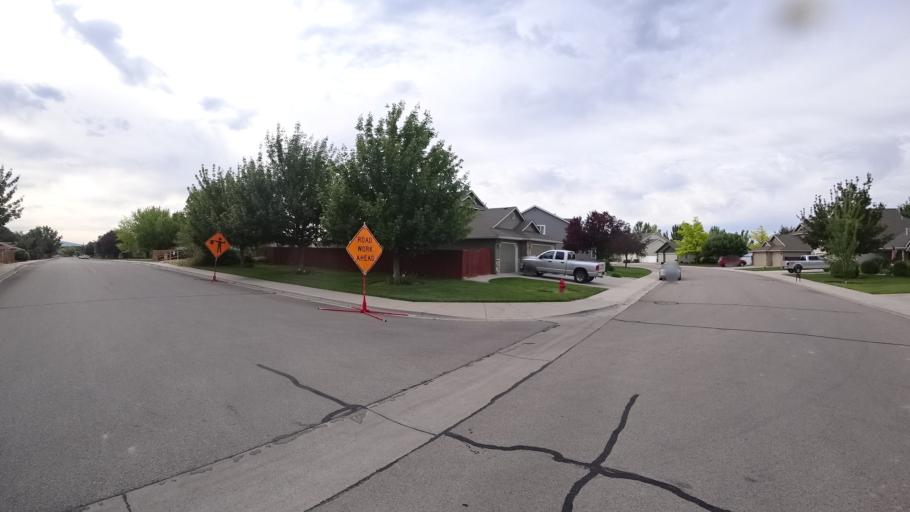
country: US
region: Idaho
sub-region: Ada County
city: Meridian
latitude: 43.5860
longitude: -116.3981
